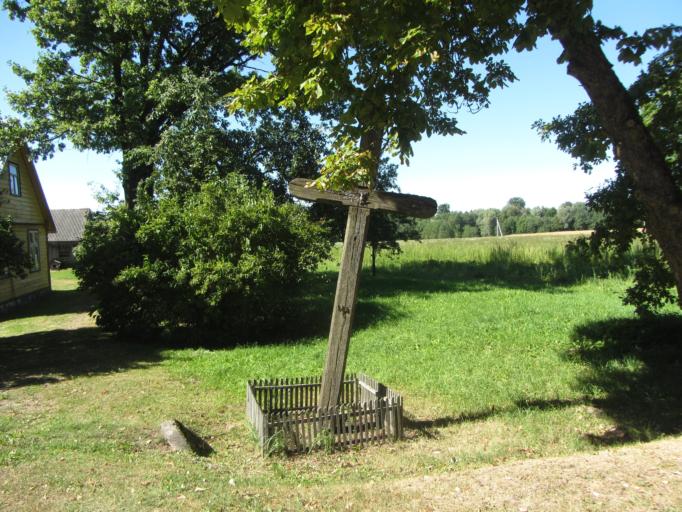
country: LT
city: Kupiskis
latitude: 55.8832
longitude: 25.0034
